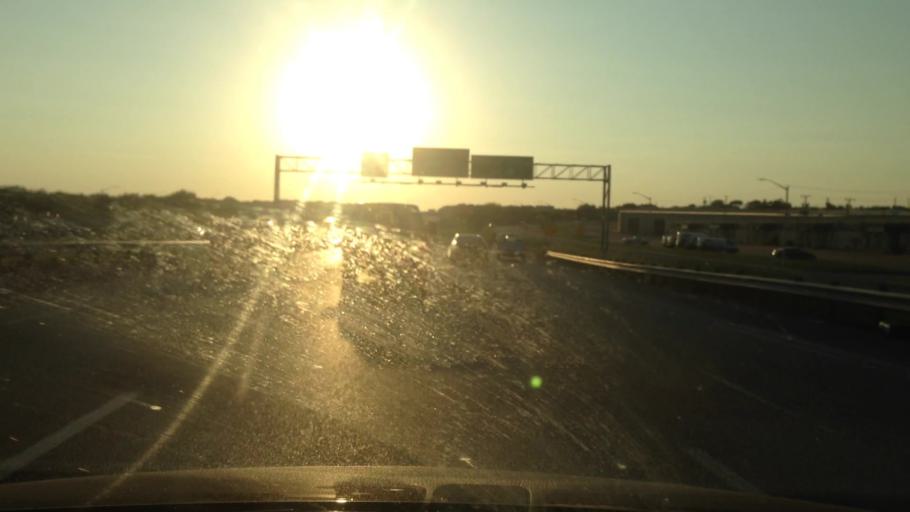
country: US
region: Texas
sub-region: Tarrant County
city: Forest Hill
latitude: 32.6939
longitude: -97.2461
